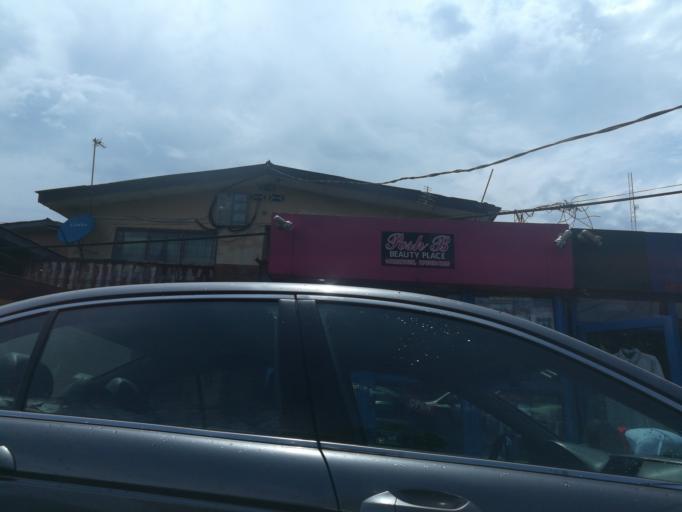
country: NG
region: Lagos
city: Somolu
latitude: 6.5613
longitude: 3.3701
